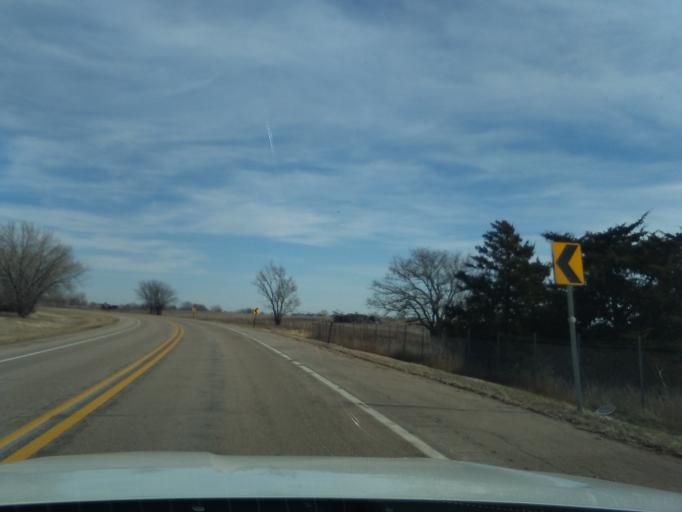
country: US
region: Nebraska
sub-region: Saline County
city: Friend
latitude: 40.6412
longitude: -97.4283
